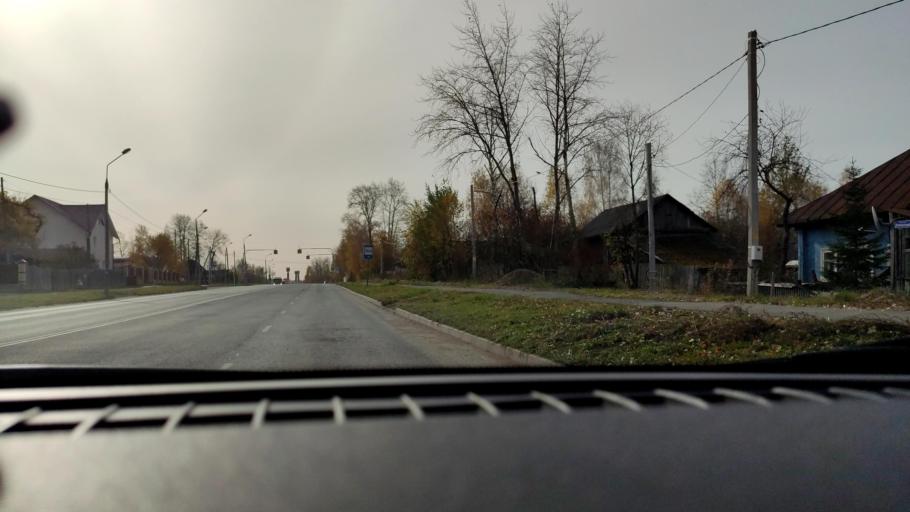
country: RU
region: Perm
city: Polazna
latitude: 58.1249
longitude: 56.4050
